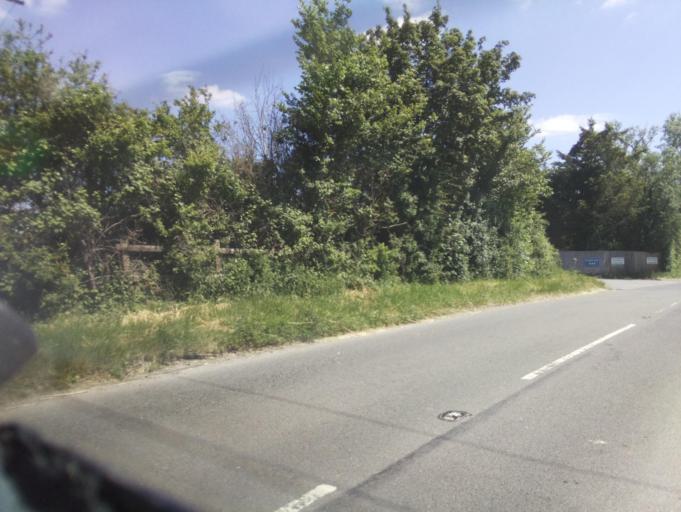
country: GB
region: England
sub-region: Wiltshire
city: Royal Wootton Bassett
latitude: 51.5283
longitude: -1.8939
